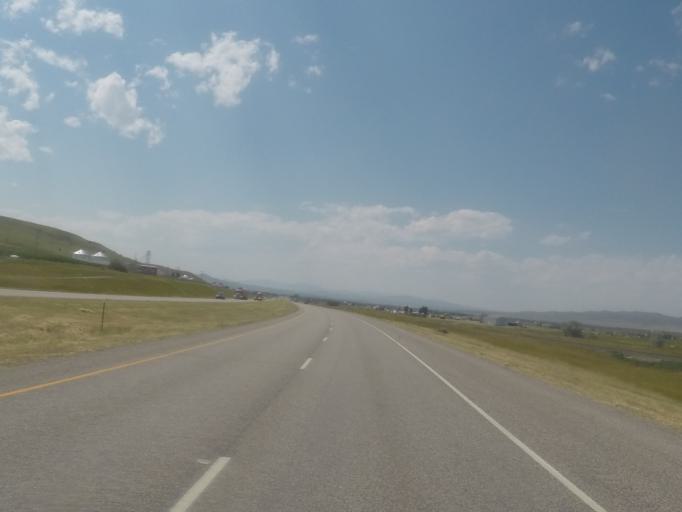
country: US
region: Montana
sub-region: Gallatin County
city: Three Forks
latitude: 45.8901
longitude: -111.4625
